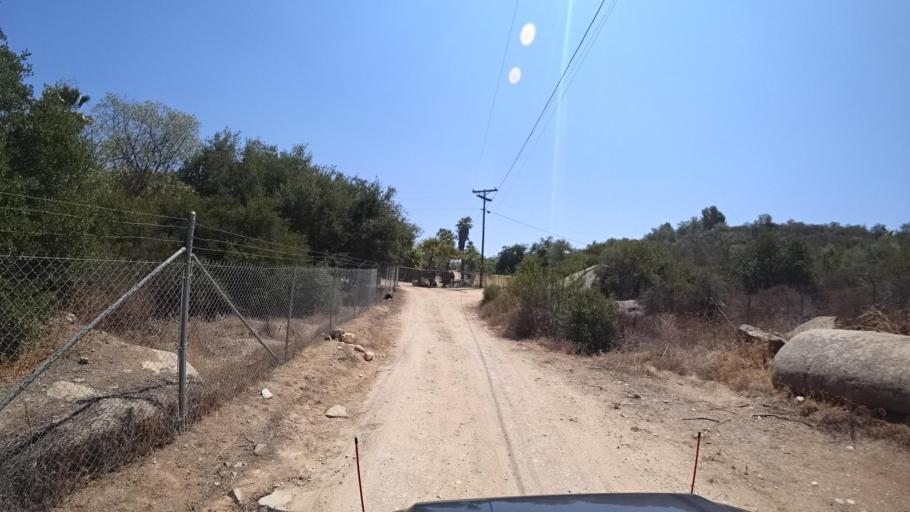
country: US
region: California
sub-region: San Diego County
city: Fallbrook
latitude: 33.4520
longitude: -117.2691
